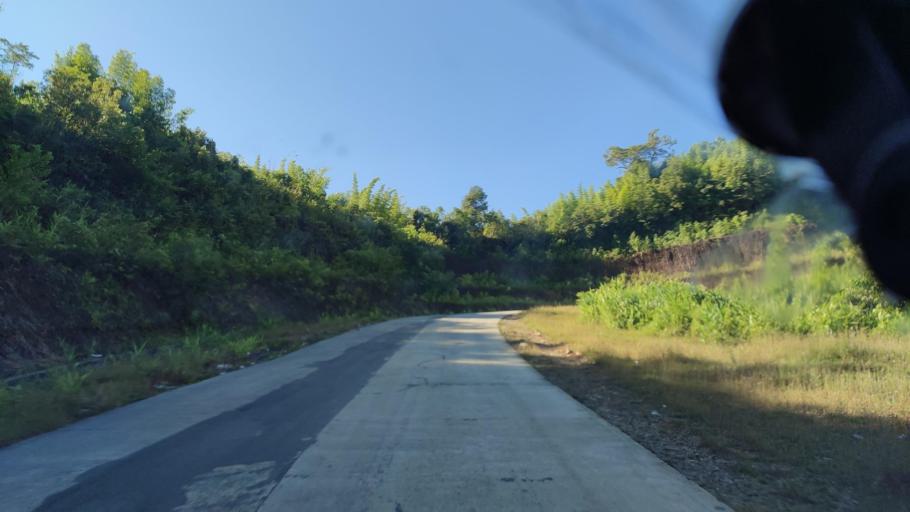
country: MM
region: Rakhine
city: Sittwe
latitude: 19.9311
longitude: 93.7711
